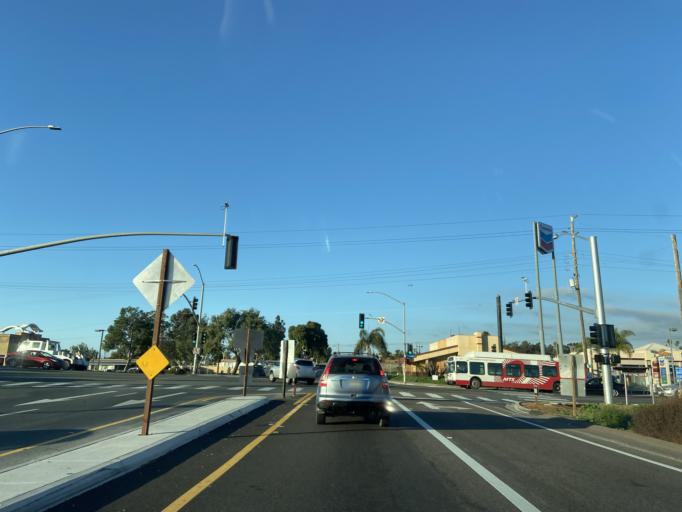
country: US
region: California
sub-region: San Diego County
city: Imperial Beach
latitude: 32.5761
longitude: -117.0804
